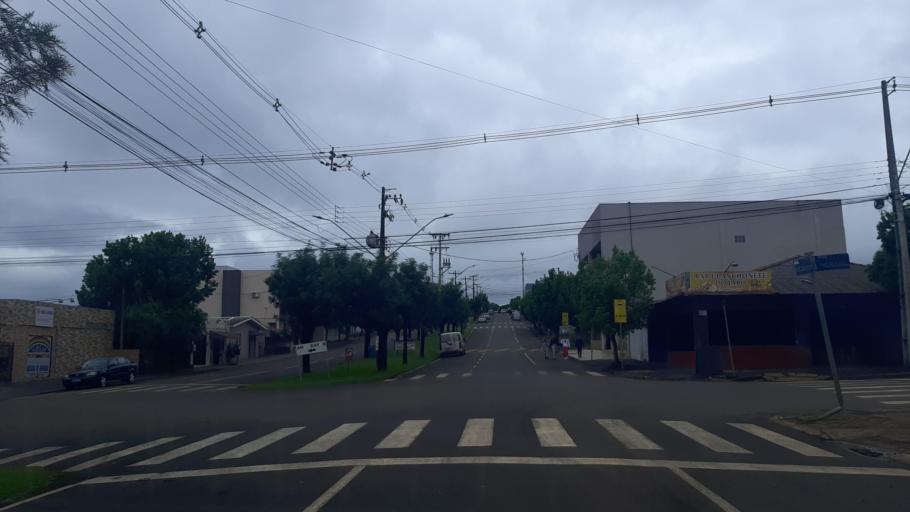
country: BR
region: Parana
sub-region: Ampere
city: Ampere
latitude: -25.9212
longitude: -53.4716
